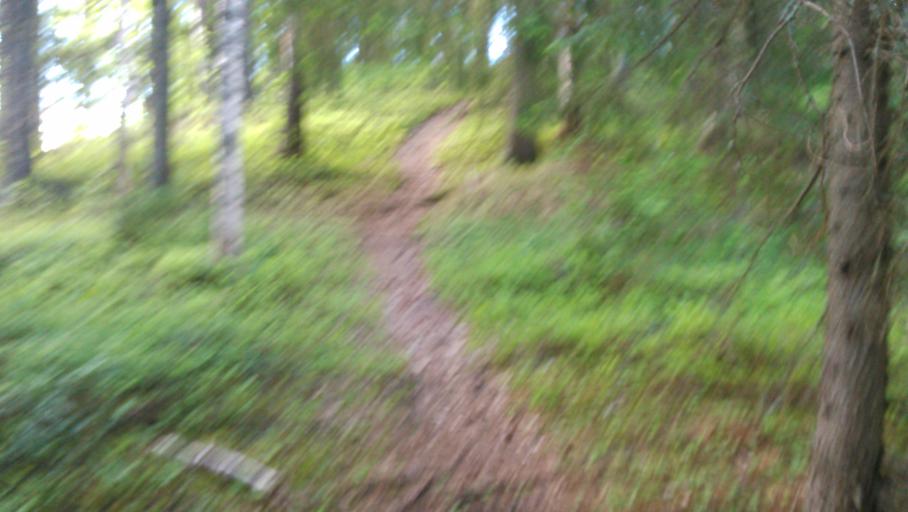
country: SE
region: Vaesterbotten
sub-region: Vannas Kommun
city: Vannasby
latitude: 64.0148
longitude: 19.9030
